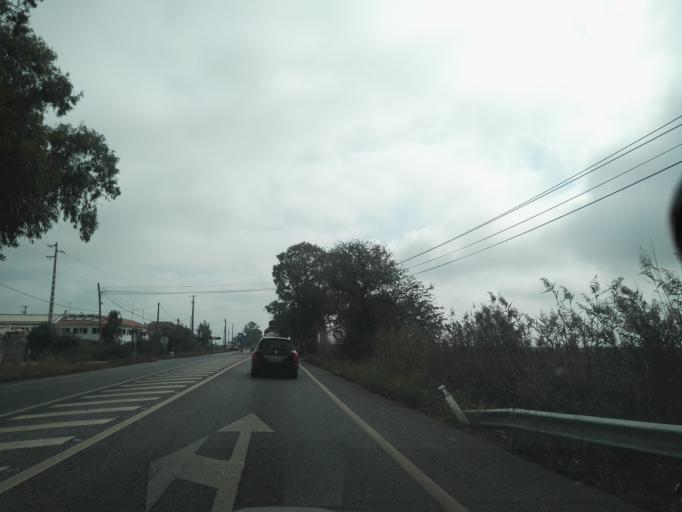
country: PT
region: Lisbon
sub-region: Vila Franca de Xira
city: Vila Franca de Xira
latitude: 38.9433
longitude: -8.9488
